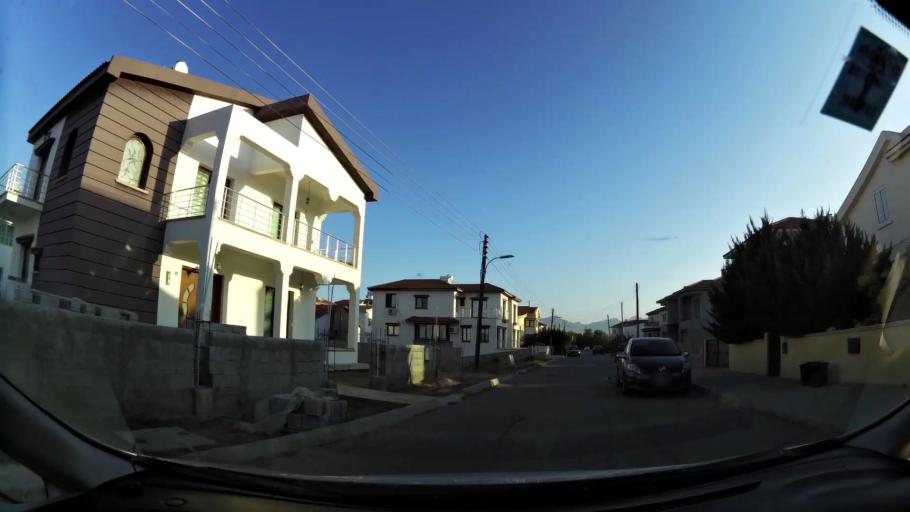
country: CY
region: Lefkosia
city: Nicosia
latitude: 35.1935
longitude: 33.3166
